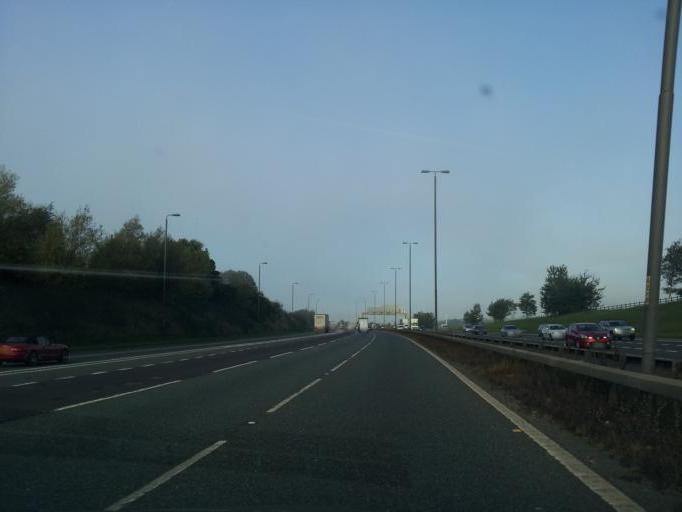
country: GB
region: England
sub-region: City and Borough of Leeds
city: Lofthouse
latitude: 53.7339
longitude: -1.5272
